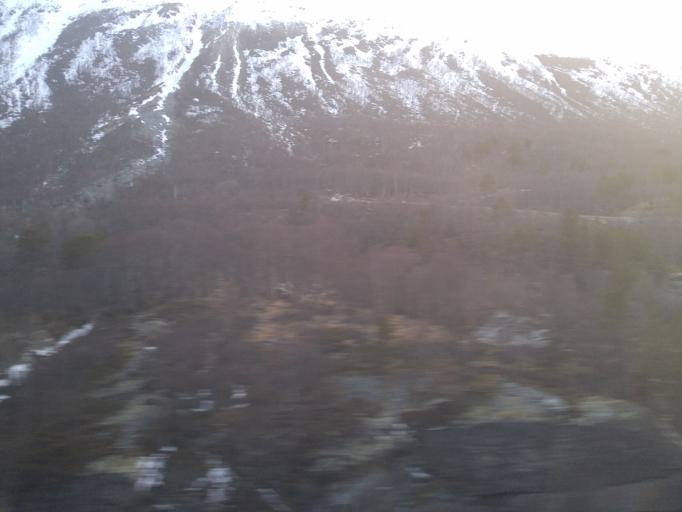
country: NO
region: Sor-Trondelag
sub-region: Oppdal
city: Oppdal
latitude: 62.4545
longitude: 9.5736
